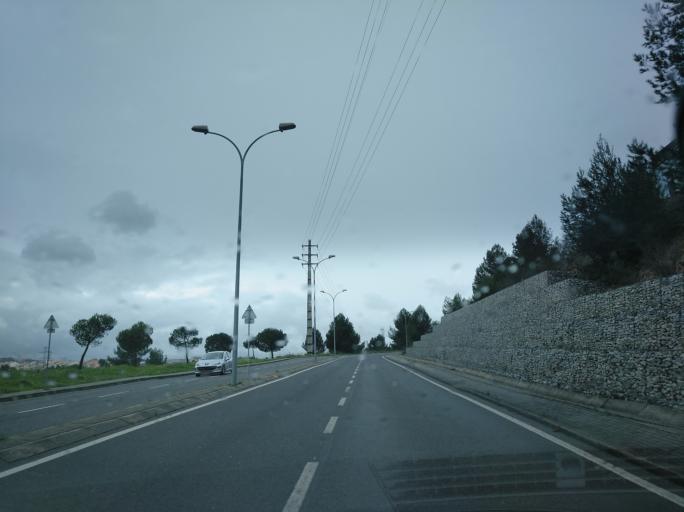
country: PT
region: Lisbon
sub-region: Odivelas
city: Odivelas
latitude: 38.7839
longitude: -9.1944
